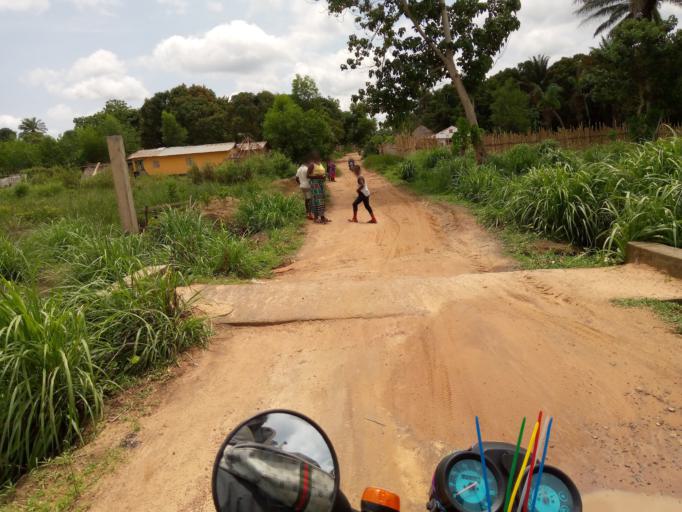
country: SL
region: Western Area
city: Waterloo
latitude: 8.3323
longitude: -12.9412
